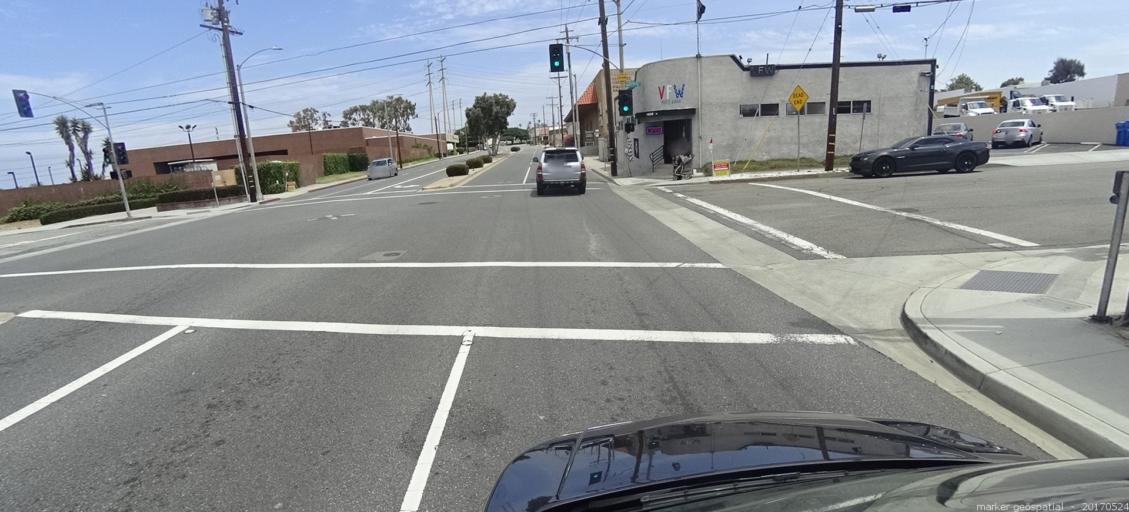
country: US
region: California
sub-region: Los Angeles County
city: Redondo Beach
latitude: 33.8509
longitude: -118.3912
